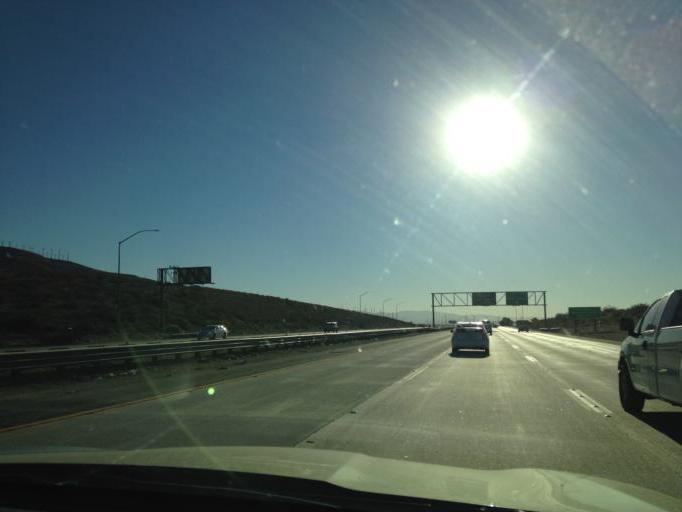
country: US
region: California
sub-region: Riverside County
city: Cabazon
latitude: 33.9237
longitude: -116.6895
